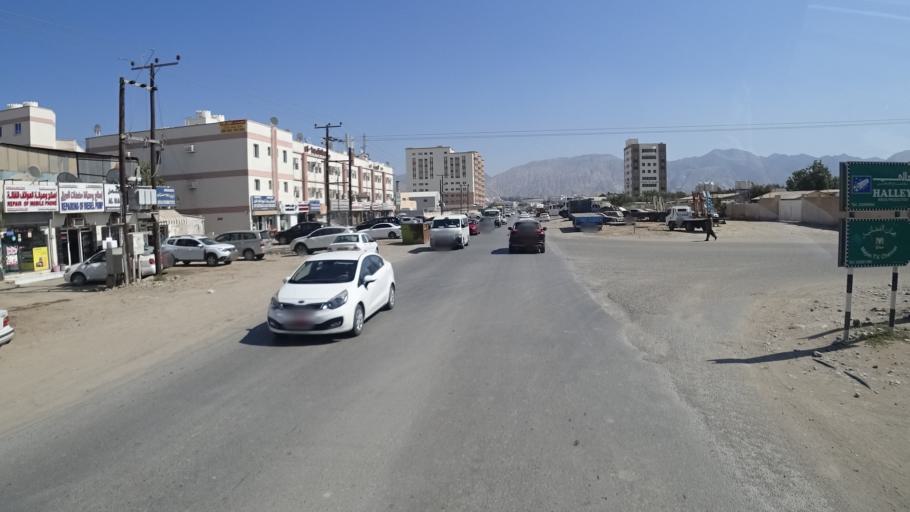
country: OM
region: Muhafazat Masqat
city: Bawshar
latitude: 23.5741
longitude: 58.3730
